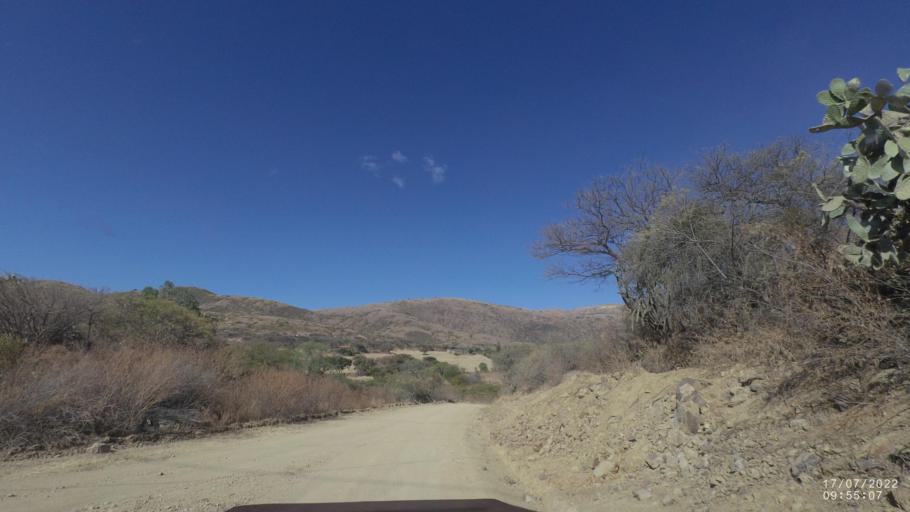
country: BO
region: Cochabamba
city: Capinota
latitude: -17.5931
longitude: -66.1900
